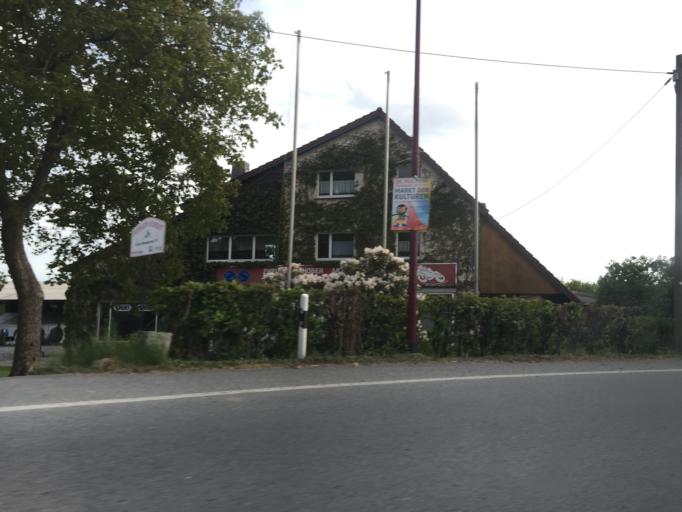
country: DE
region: Saxony
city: Hohnstein
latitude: 50.9866
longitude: 14.0745
